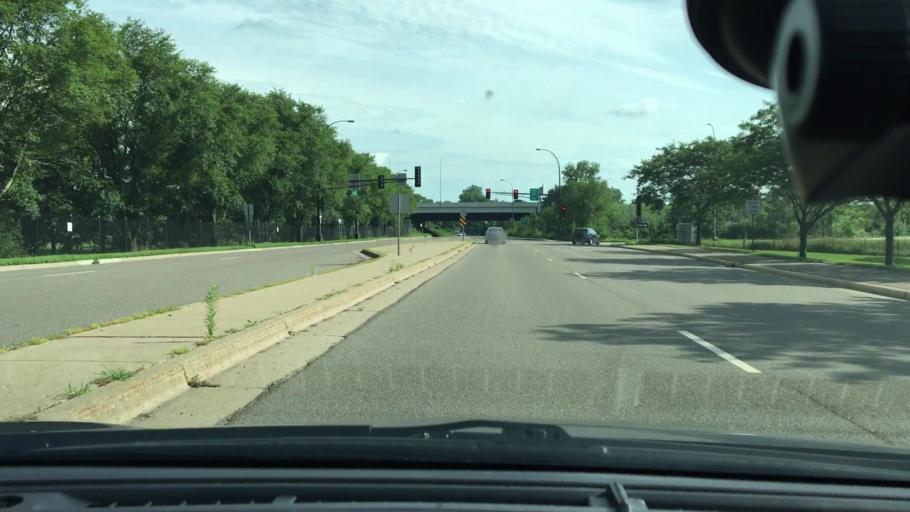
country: US
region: Minnesota
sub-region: Hennepin County
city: Saint Louis Park
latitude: 44.9763
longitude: -93.3908
